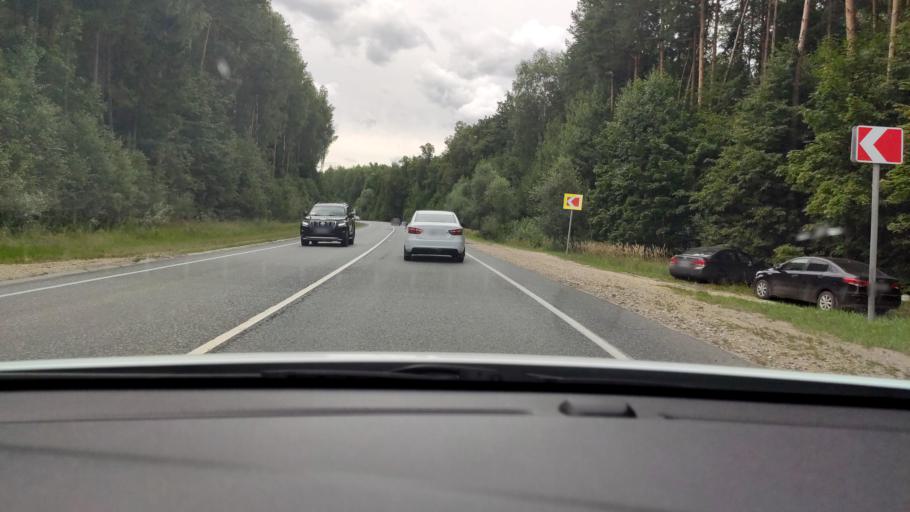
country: RU
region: Tatarstan
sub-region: Zelenodol'skiy Rayon
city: Zelenodolsk
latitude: 55.8981
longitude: 48.5591
